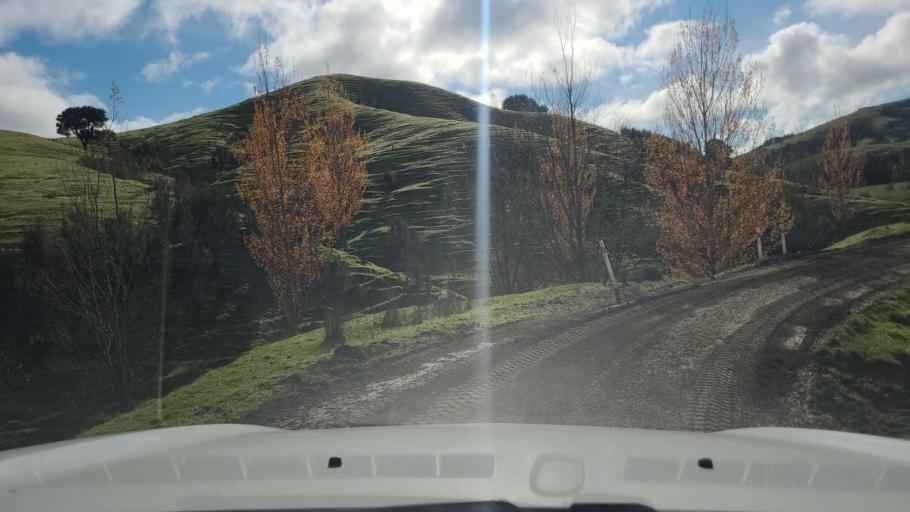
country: NZ
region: Wellington
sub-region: South Wairarapa District
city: Waipawa
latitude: -41.2401
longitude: 175.6851
